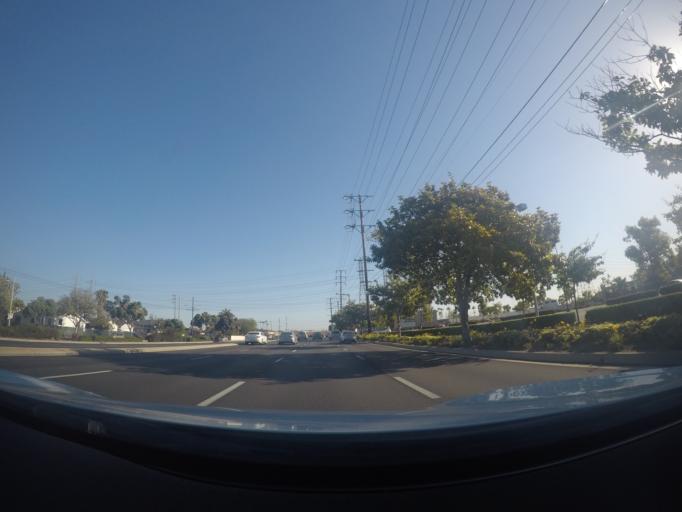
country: US
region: California
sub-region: Los Angeles County
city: Torrance
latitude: 33.8554
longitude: -118.3536
